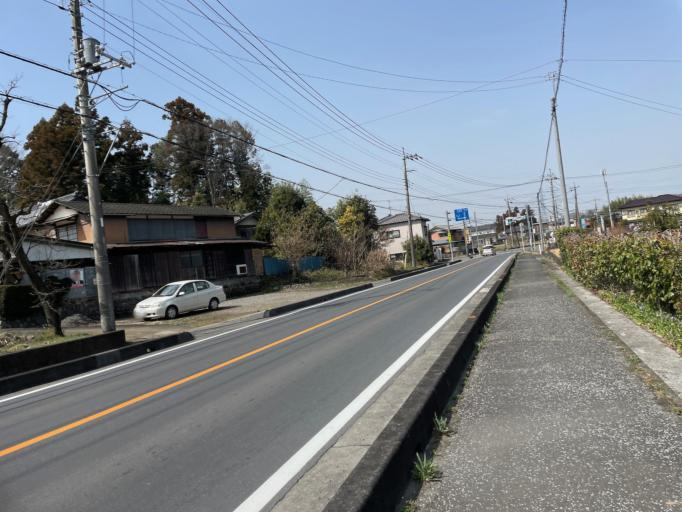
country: JP
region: Saitama
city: Ogawa
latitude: 36.0881
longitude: 139.2808
